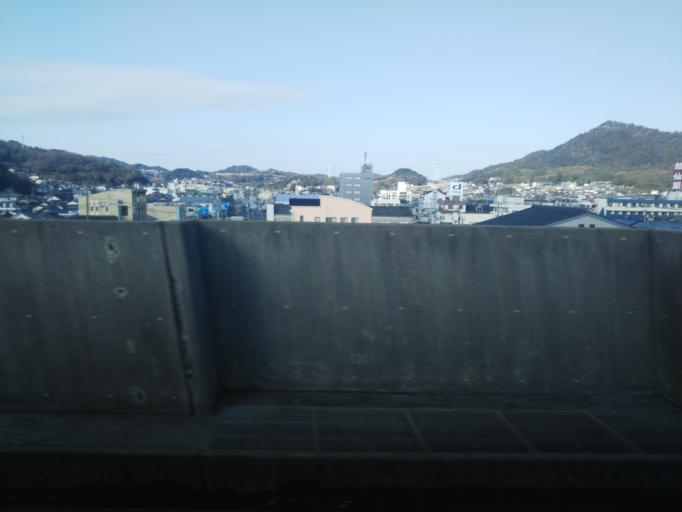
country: JP
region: Okayama
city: Kurashiki
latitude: 34.4571
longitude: 133.8070
